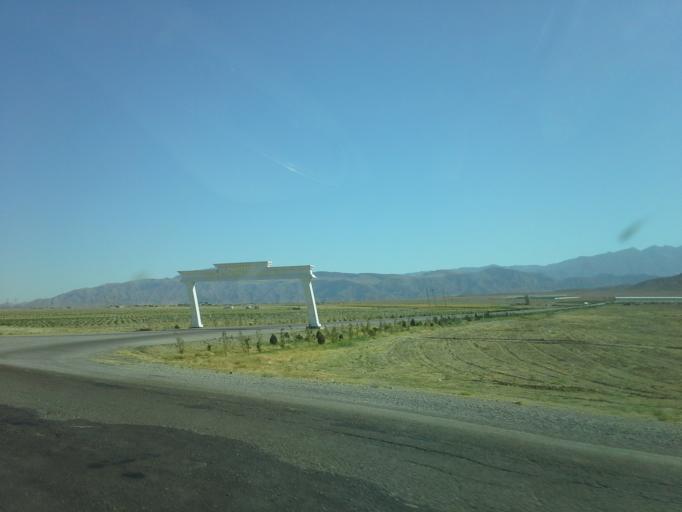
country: TM
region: Ahal
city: Baharly
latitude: 38.4515
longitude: 57.3702
